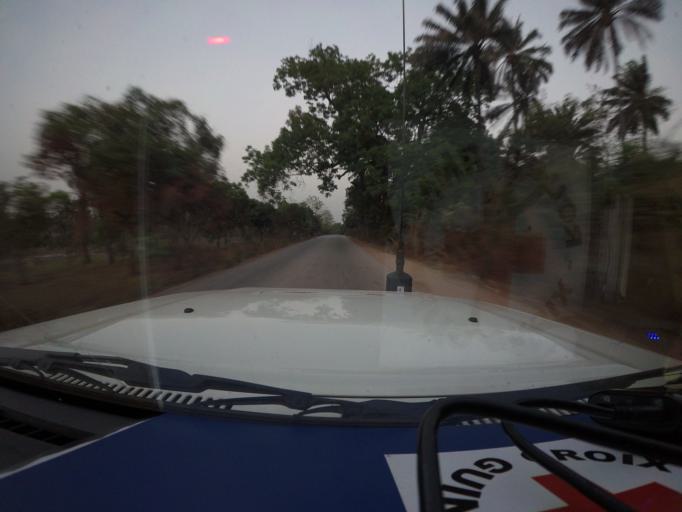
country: GN
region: Kindia
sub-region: Kindia
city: Kindia
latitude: 9.9436
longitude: -12.9640
